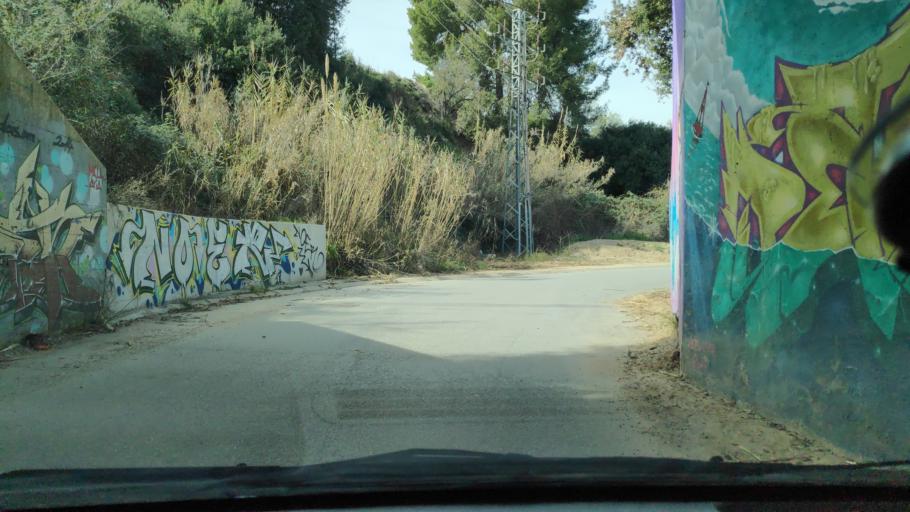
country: ES
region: Catalonia
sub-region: Provincia de Barcelona
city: Rubi
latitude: 41.5068
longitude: 2.0313
